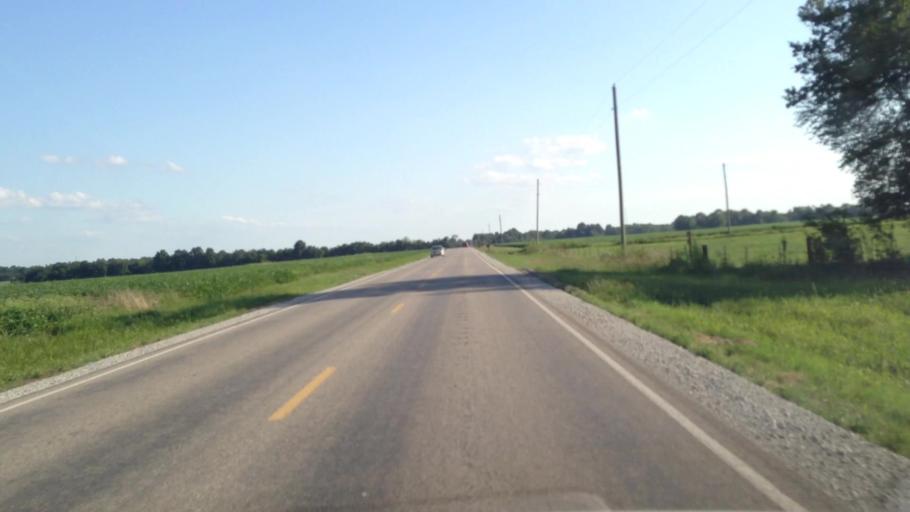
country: US
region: Kansas
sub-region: Crawford County
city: Pittsburg
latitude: 37.3606
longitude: -94.6315
